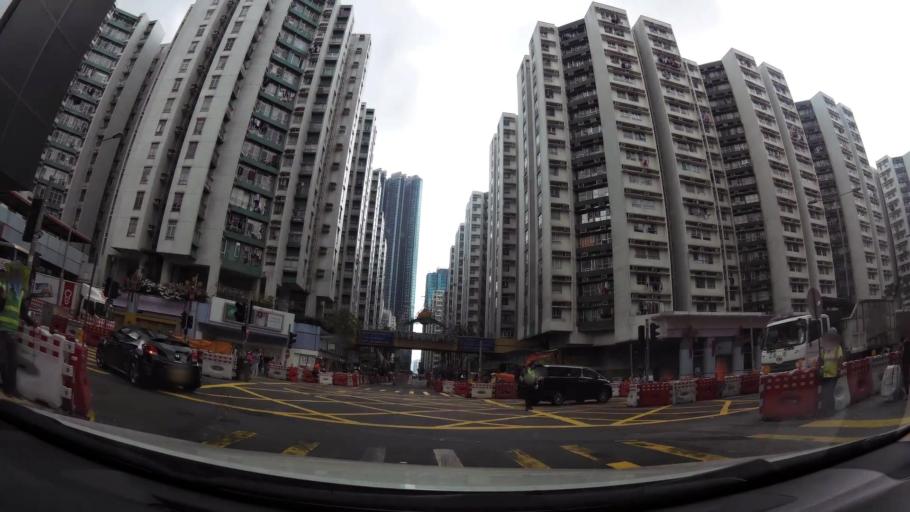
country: HK
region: Kowloon City
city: Kowloon
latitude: 22.3057
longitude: 114.1886
